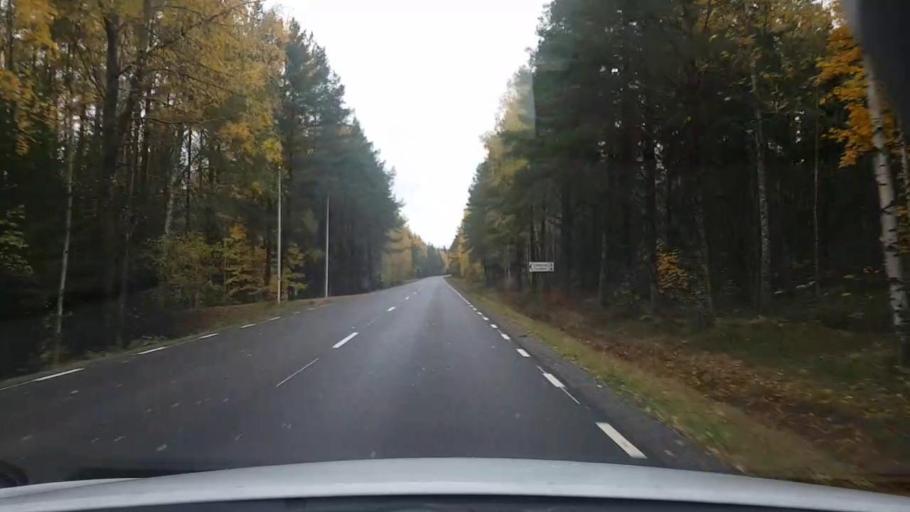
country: SE
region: OErebro
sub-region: Laxa Kommun
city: Laxa
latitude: 58.7979
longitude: 14.5423
